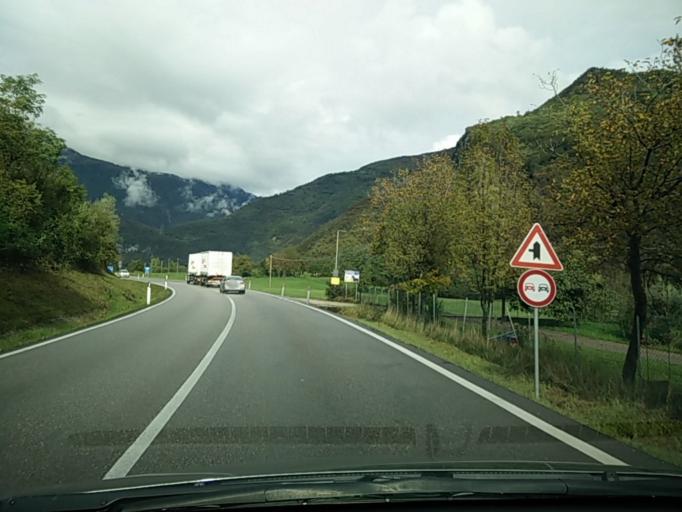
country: IT
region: Veneto
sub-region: Provincia di Treviso
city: Segusino
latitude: 45.9227
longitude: 11.9455
